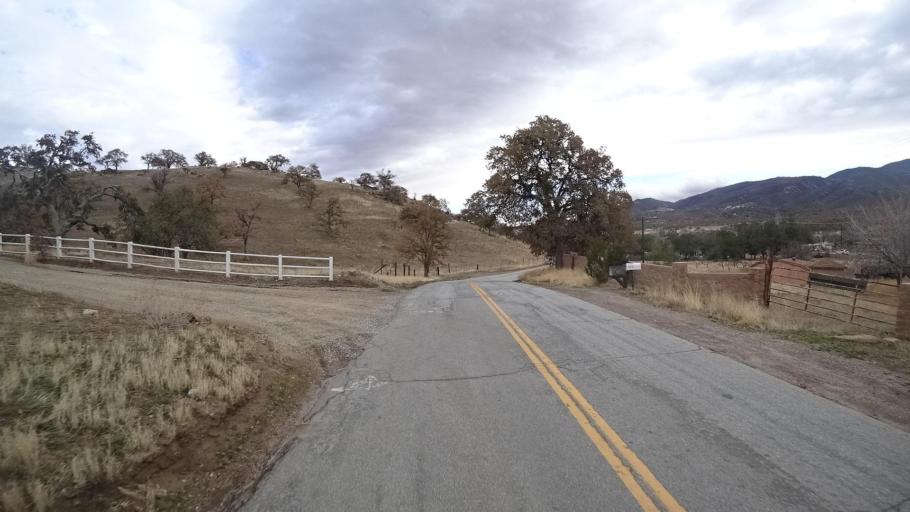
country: US
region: California
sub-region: Kern County
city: Golden Hills
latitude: 35.1130
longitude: -118.5191
